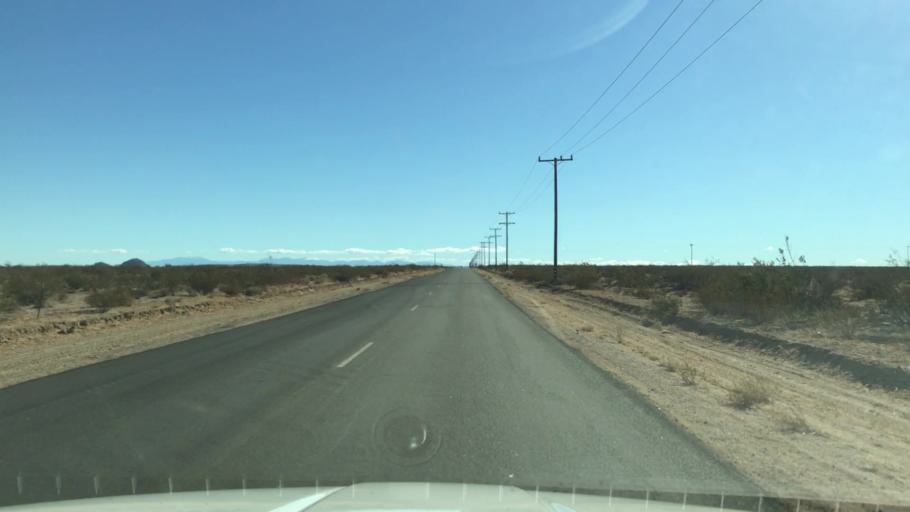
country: US
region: California
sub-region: Kern County
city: California City
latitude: 35.1879
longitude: -117.9858
